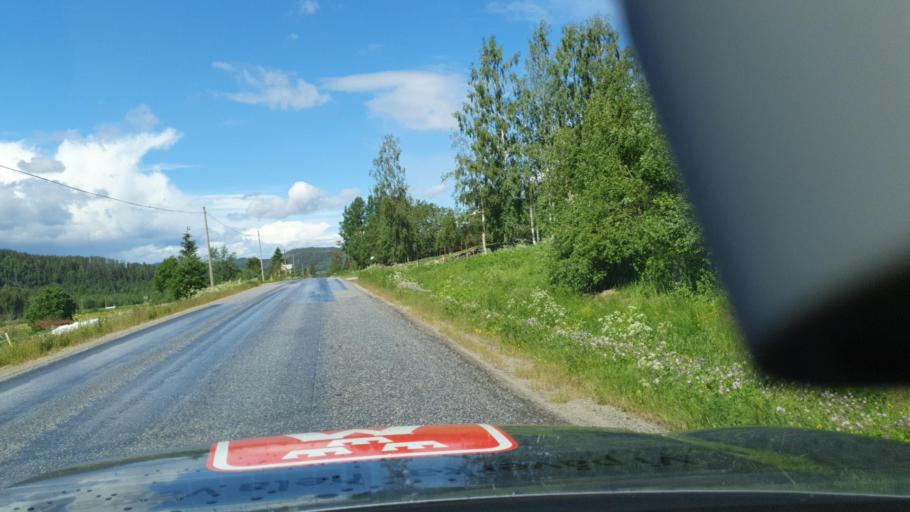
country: SE
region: Vaesternorrland
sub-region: OErnskoeldsviks Kommun
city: Bredbyn
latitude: 63.3427
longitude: 18.0103
